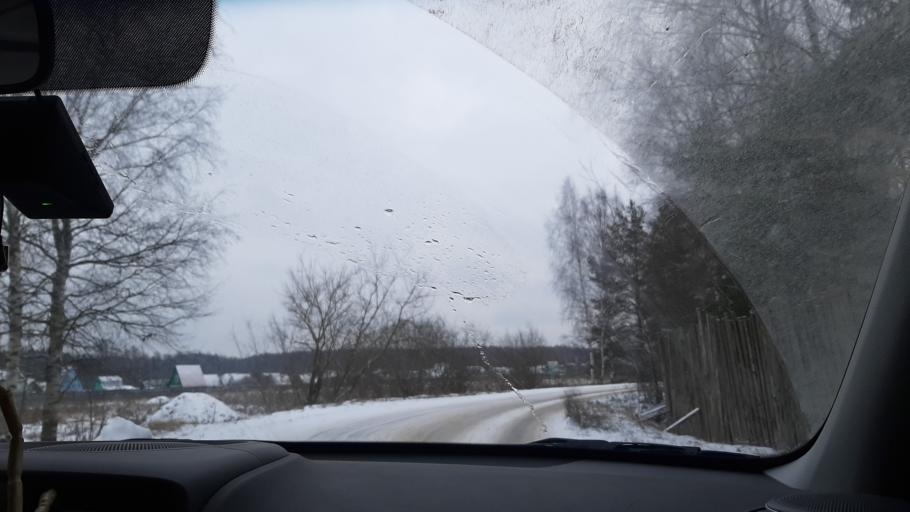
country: RU
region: Ivanovo
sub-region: Gorod Ivanovo
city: Ivanovo
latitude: 56.9329
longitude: 40.9739
